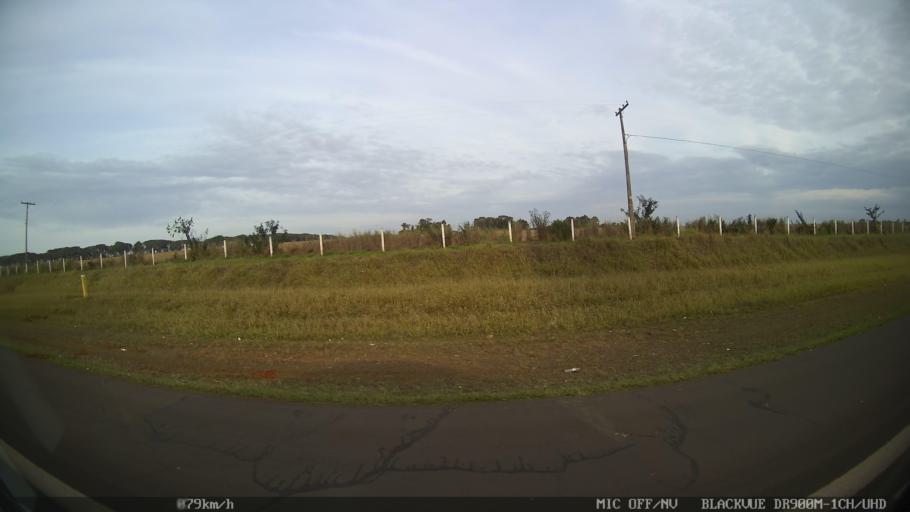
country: BR
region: Sao Paulo
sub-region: Iracemapolis
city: Iracemapolis
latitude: -22.6530
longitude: -47.5175
